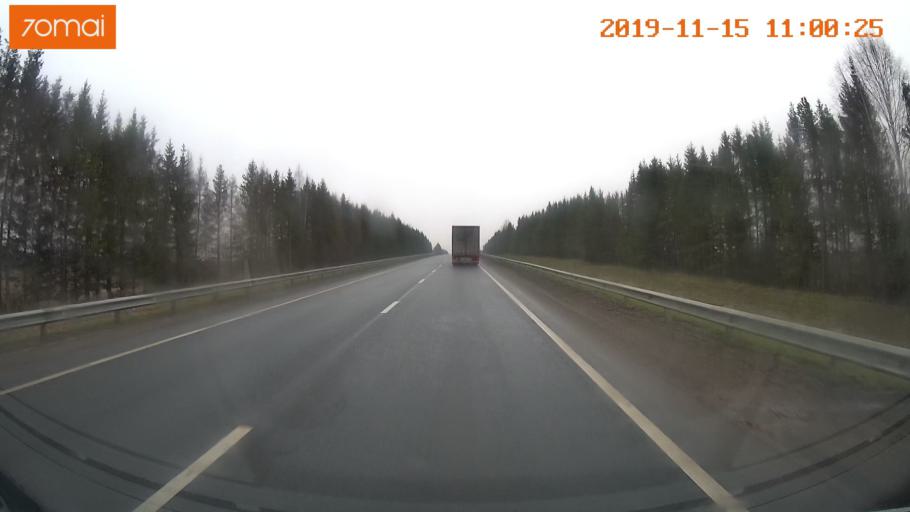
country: RU
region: Vologda
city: Chebsara
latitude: 59.1373
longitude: 38.8987
